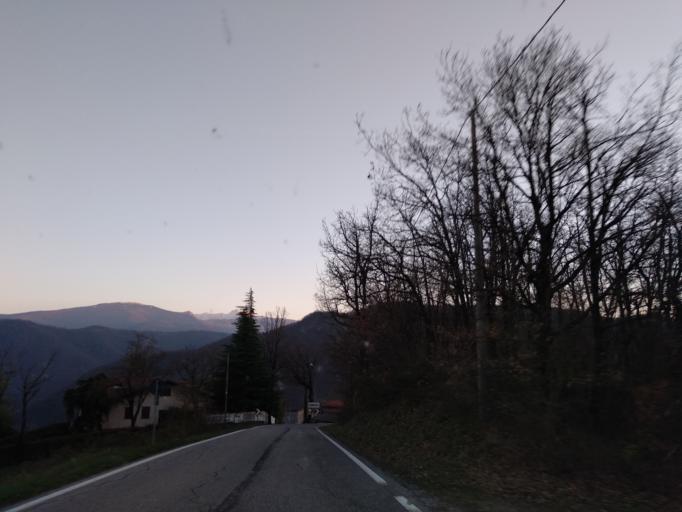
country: IT
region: Emilia-Romagna
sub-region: Provincia di Reggio Emilia
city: Castelnovo ne'Monti
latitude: 44.4033
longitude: 10.3983
